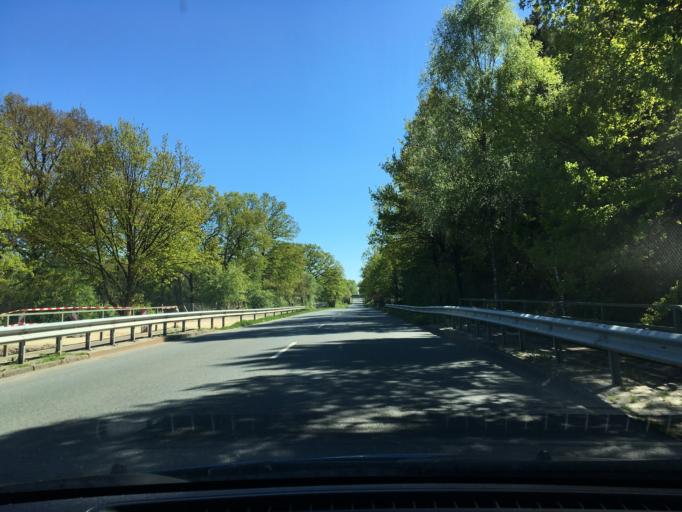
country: DE
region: Lower Saxony
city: Munster
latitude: 53.0100
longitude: 10.0492
